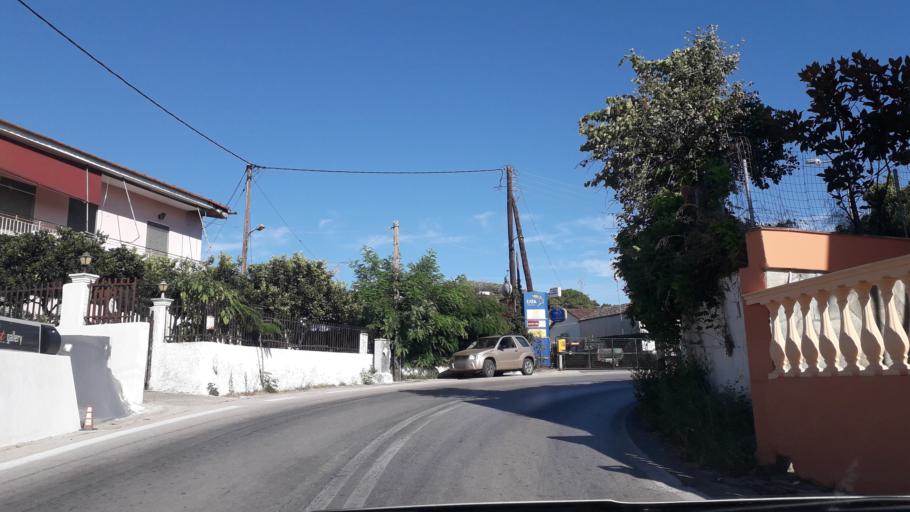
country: GR
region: Ionian Islands
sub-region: Nomos Kerkyras
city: Agios Matthaios
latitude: 39.4672
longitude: 19.9120
